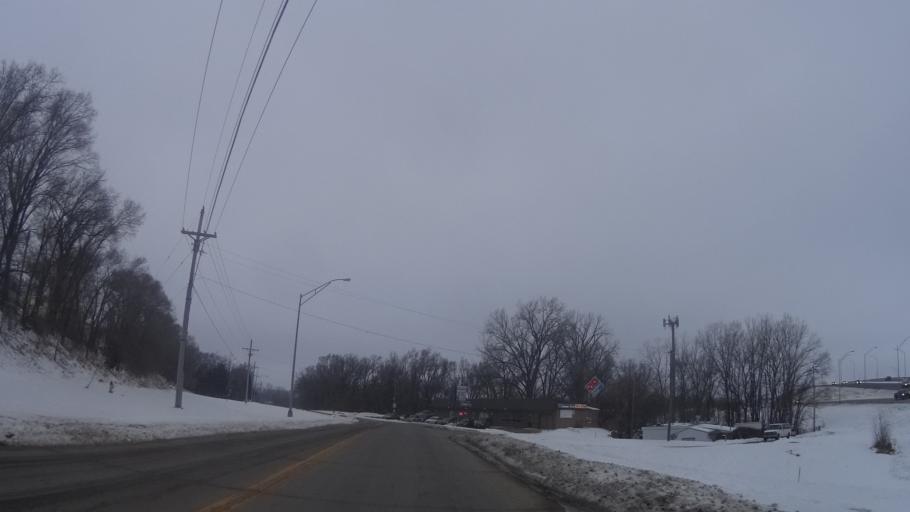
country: US
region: Nebraska
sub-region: Sarpy County
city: Offutt Air Force Base
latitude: 41.1398
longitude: -95.9222
